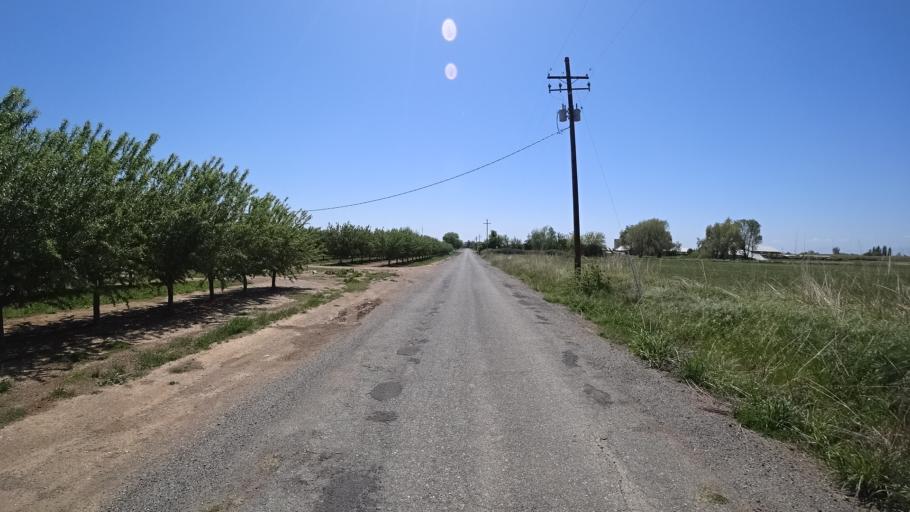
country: US
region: California
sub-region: Glenn County
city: Orland
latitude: 39.7770
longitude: -122.1503
